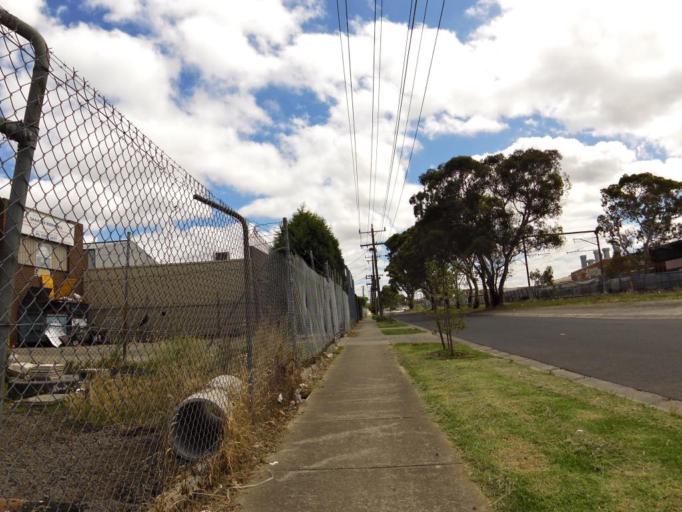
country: AU
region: Victoria
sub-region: Moreland
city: Fawkner
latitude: -37.7039
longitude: 144.9589
